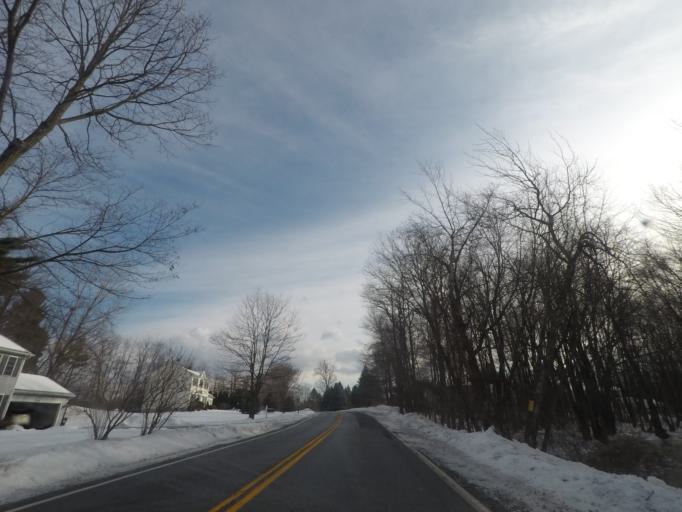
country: US
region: New York
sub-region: Saratoga County
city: Country Knolls
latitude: 42.8745
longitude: -73.7578
